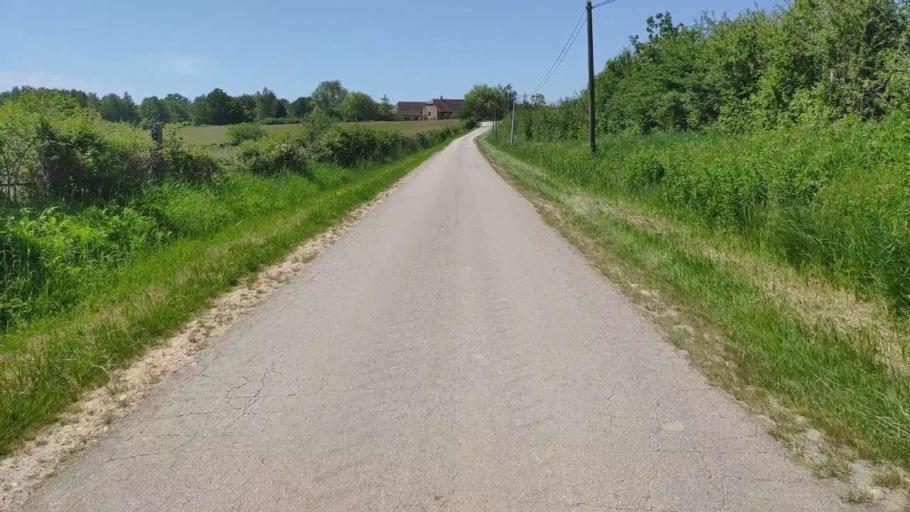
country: FR
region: Franche-Comte
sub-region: Departement du Jura
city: Bletterans
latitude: 46.7728
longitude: 5.4036
